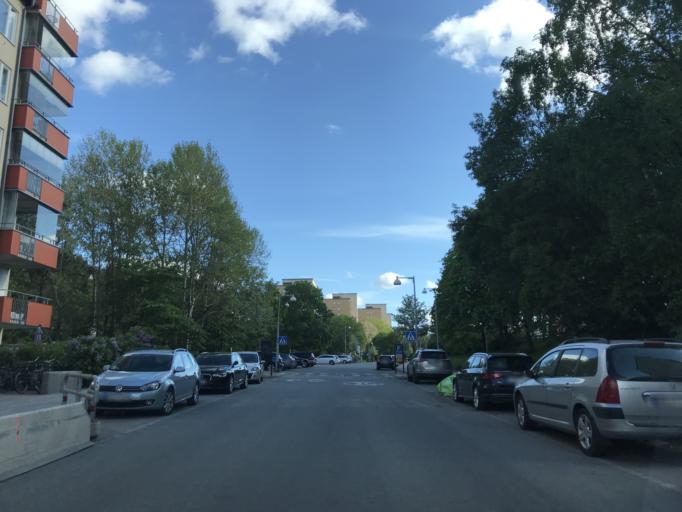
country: SE
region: Stockholm
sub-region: Solna Kommun
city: Solna
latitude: 59.3504
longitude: 17.9965
